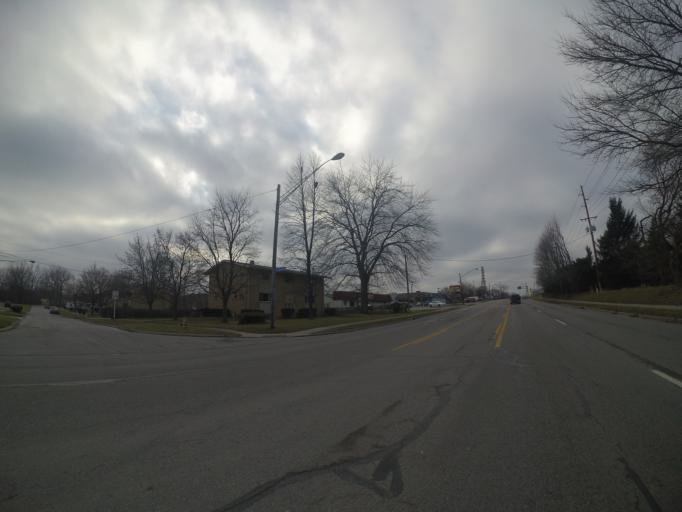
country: US
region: Ohio
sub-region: Lucas County
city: Oregon
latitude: 41.6439
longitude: -83.4926
